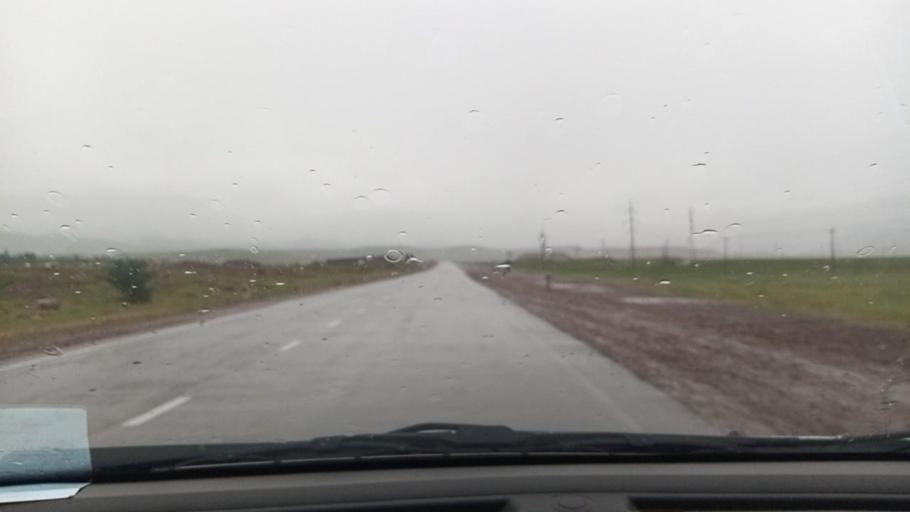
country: UZ
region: Toshkent
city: Angren
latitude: 41.0411
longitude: 70.1518
